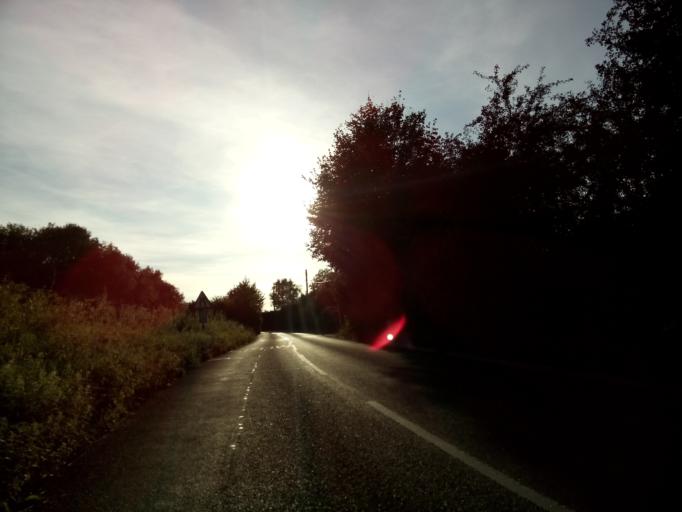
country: GB
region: England
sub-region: Suffolk
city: Bramford
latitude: 52.0307
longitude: 1.1121
